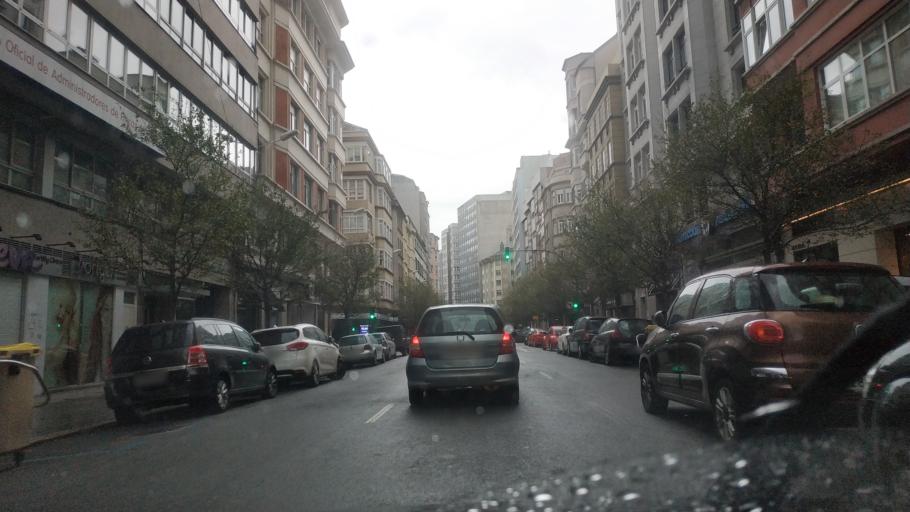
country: ES
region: Galicia
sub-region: Provincia da Coruna
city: A Coruna
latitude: 43.3636
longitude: -8.4081
